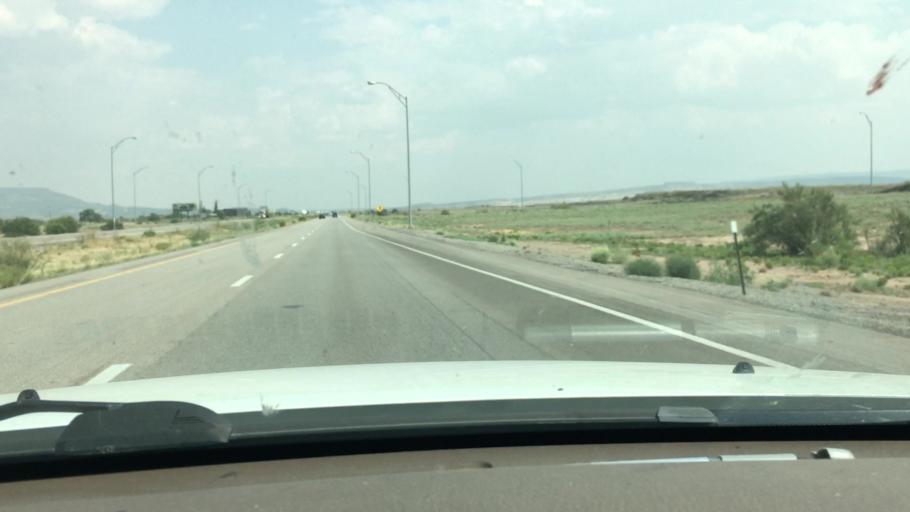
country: US
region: New Mexico
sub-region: Cibola County
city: Grants
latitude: 35.1233
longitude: -107.8288
